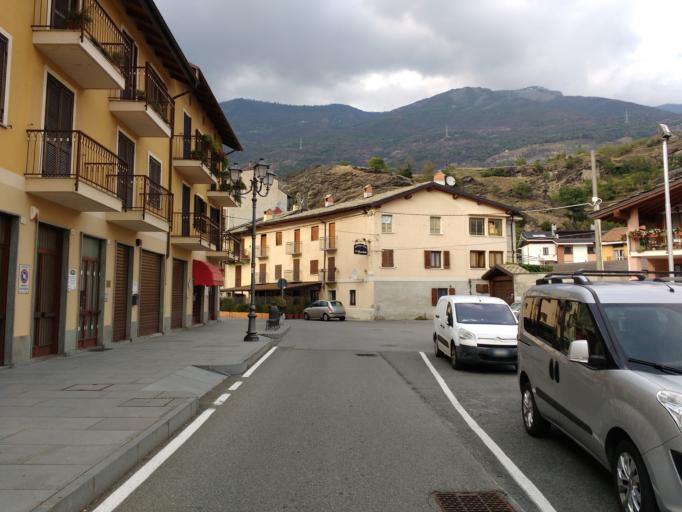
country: IT
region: Piedmont
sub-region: Provincia di Torino
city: San Giuseppe
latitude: 45.1380
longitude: 7.0446
